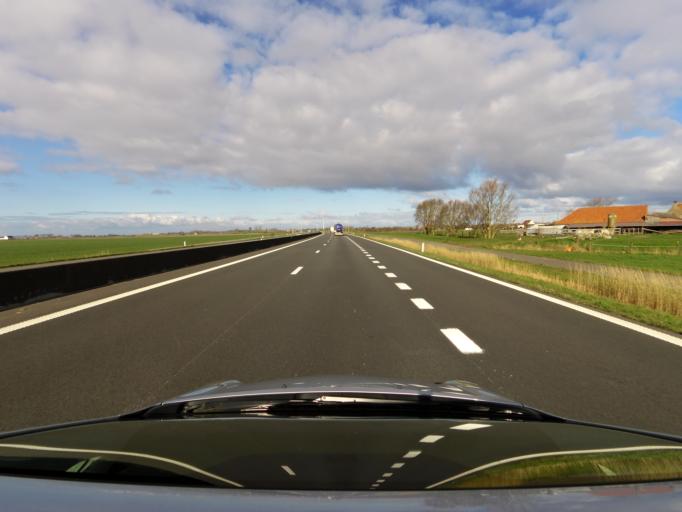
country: BE
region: Flanders
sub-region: Provincie West-Vlaanderen
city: De Panne
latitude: 51.0681
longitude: 2.6181
